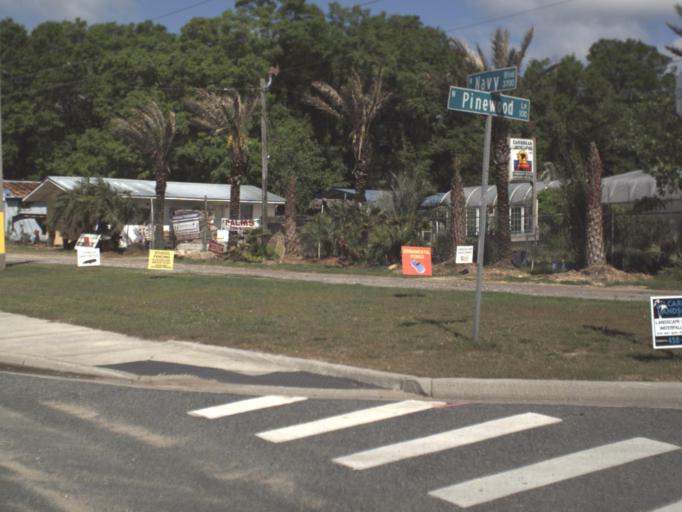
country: US
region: Florida
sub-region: Escambia County
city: West Pensacola
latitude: 30.4109
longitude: -87.2608
